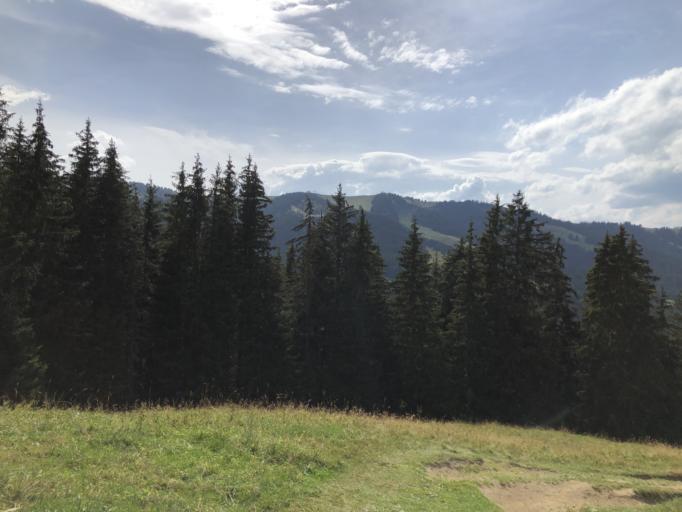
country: FR
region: Rhone-Alpes
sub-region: Departement de la Haute-Savoie
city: Megeve
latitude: 45.8252
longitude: 6.6540
